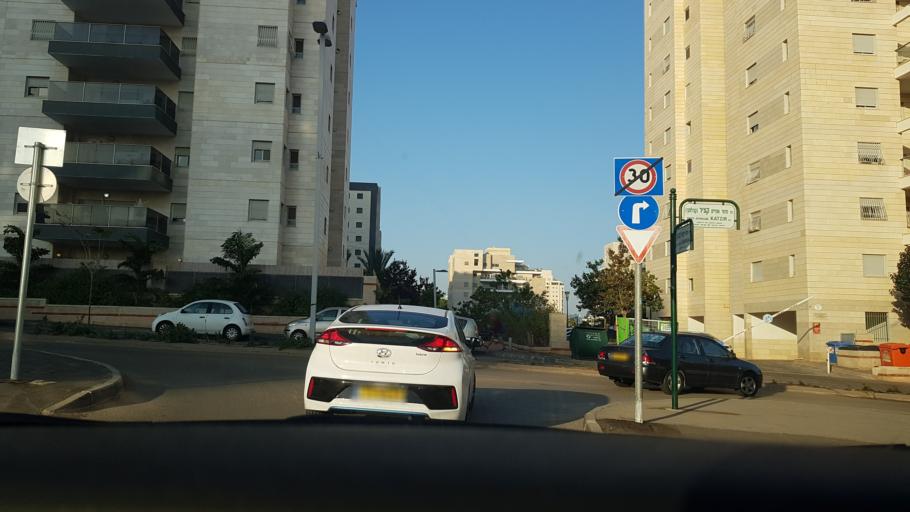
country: IL
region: Central District
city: Ness Ziona
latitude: 31.9045
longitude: 34.8213
